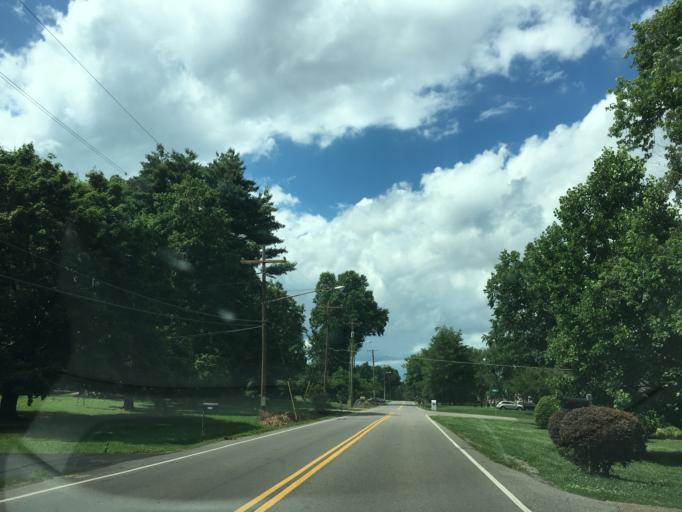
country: US
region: Tennessee
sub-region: Davidson County
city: Oak Hill
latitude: 36.0971
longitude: -86.7906
